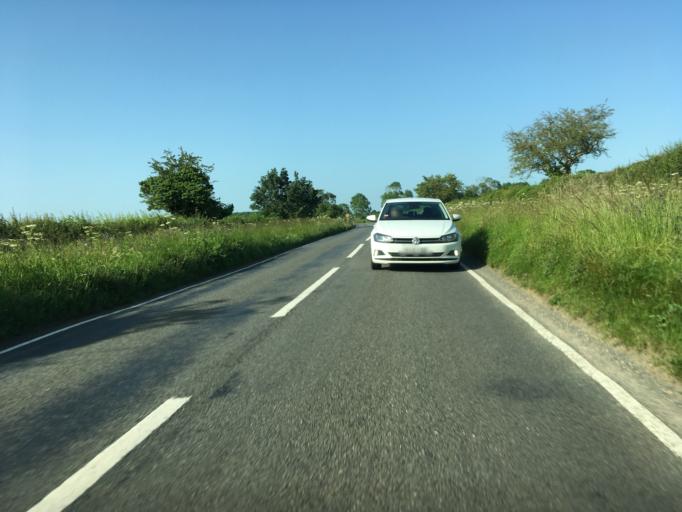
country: GB
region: England
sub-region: Oxfordshire
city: Charlbury
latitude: 51.8902
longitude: -1.4712
